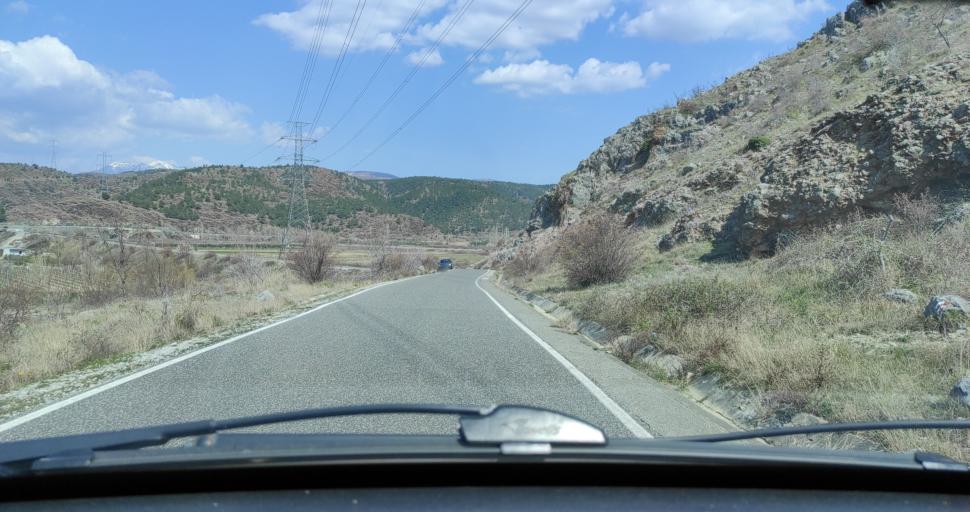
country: AL
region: Shkoder
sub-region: Rrethi i Shkodres
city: Hajmel
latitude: 41.9730
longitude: 19.6436
